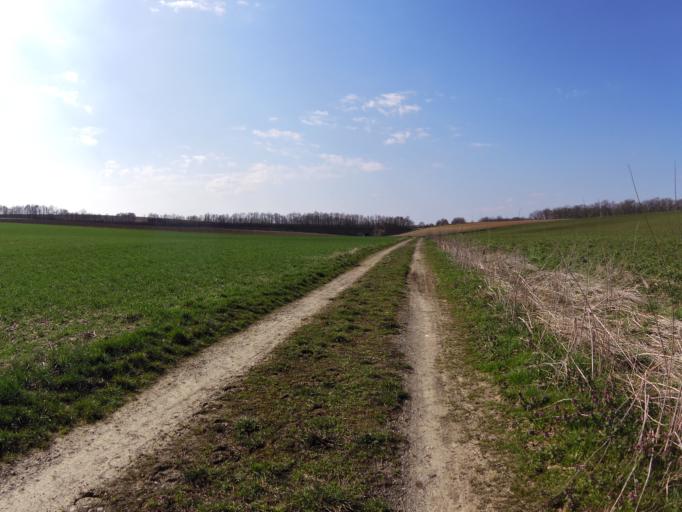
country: DE
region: Bavaria
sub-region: Regierungsbezirk Unterfranken
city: Rottendorf
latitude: 49.8002
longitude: 10.0578
